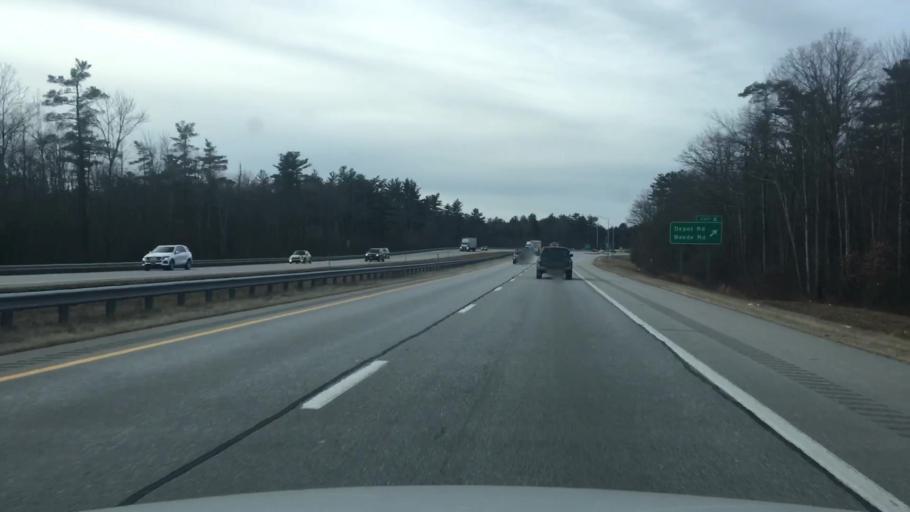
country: US
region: New Hampshire
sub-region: Rockingham County
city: Epping
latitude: 43.0256
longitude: -71.1069
